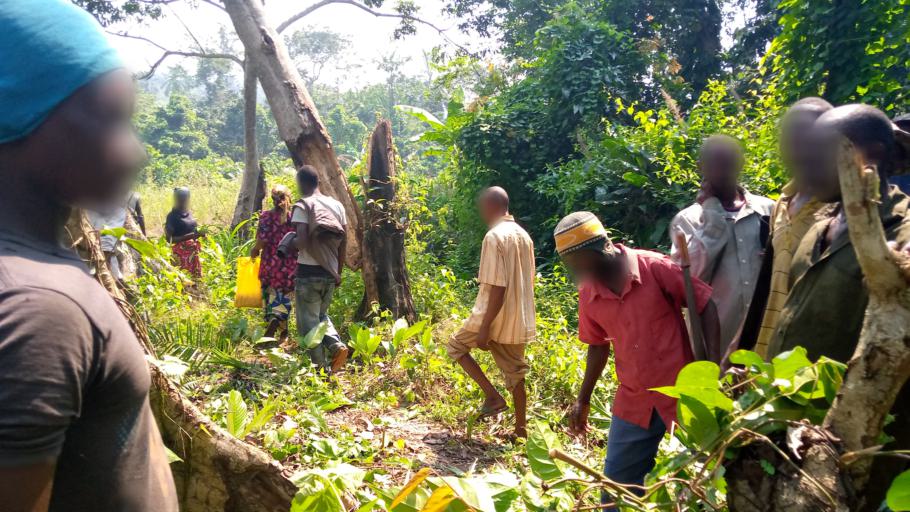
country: CD
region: Bandundu
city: Bulungu
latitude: -4.5809
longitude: 18.6437
